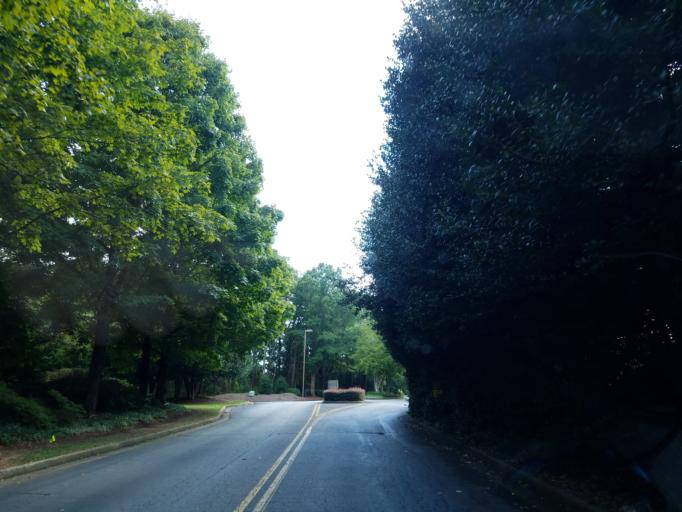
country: US
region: Georgia
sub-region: Cobb County
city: Fair Oaks
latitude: 33.9387
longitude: -84.5051
